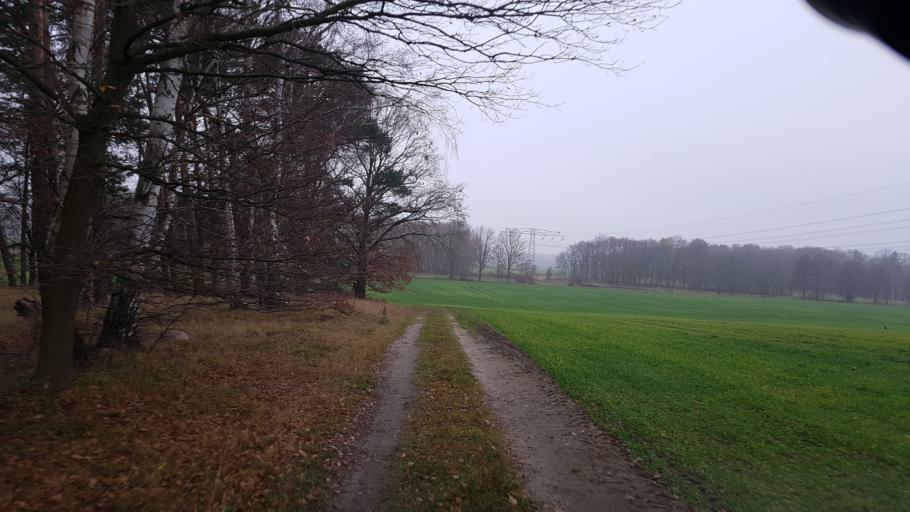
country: DE
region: Brandenburg
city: Altdobern
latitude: 51.6763
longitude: 13.9990
